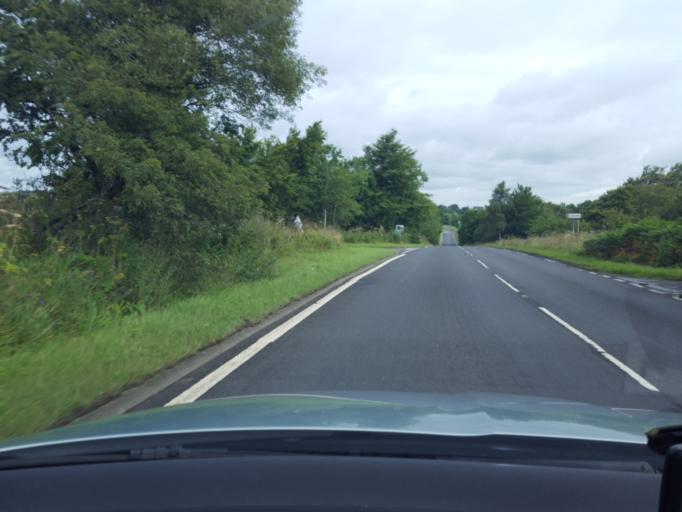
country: GB
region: Scotland
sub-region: Falkirk
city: Polmont
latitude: 55.9556
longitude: -3.6887
